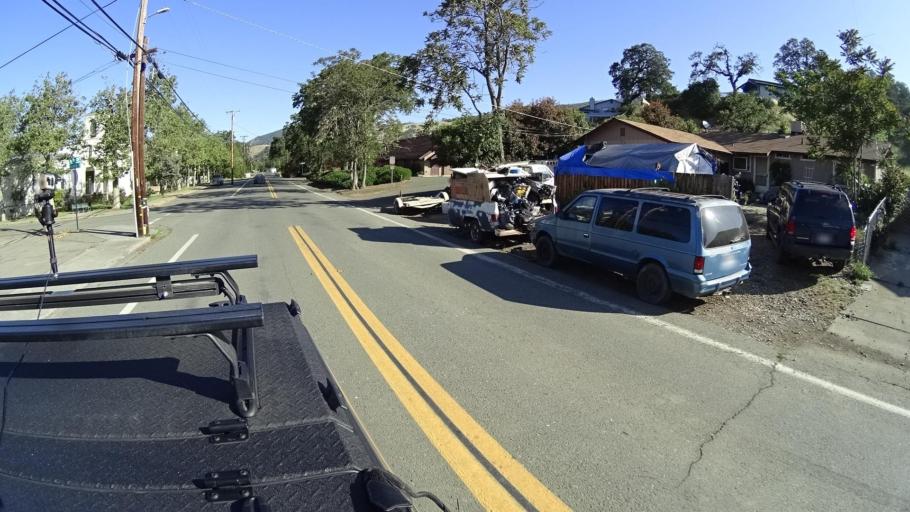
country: US
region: California
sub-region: Lake County
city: Lucerne
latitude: 39.0908
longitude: -122.7920
